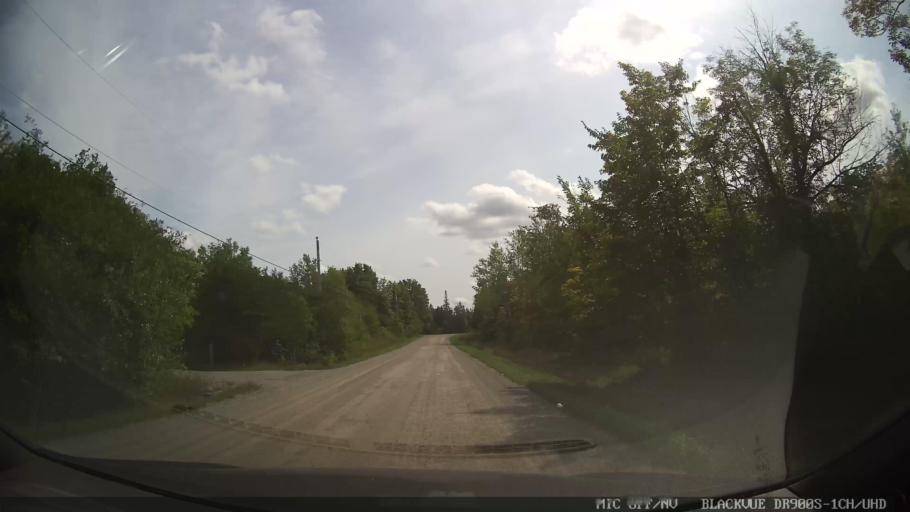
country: CA
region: Ontario
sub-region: Lanark County
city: Smiths Falls
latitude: 44.9824
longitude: -75.8820
